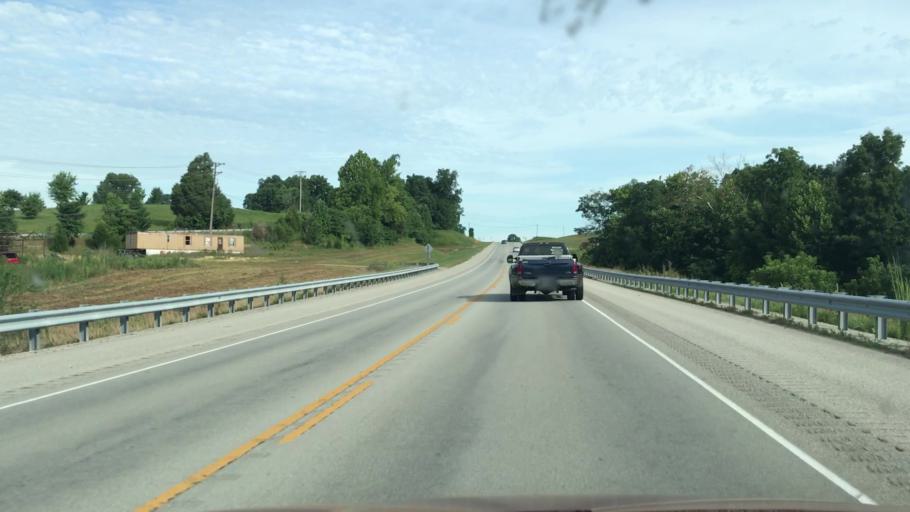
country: US
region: Kentucky
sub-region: Edmonson County
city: Brownsville
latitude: 37.1619
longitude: -86.2235
